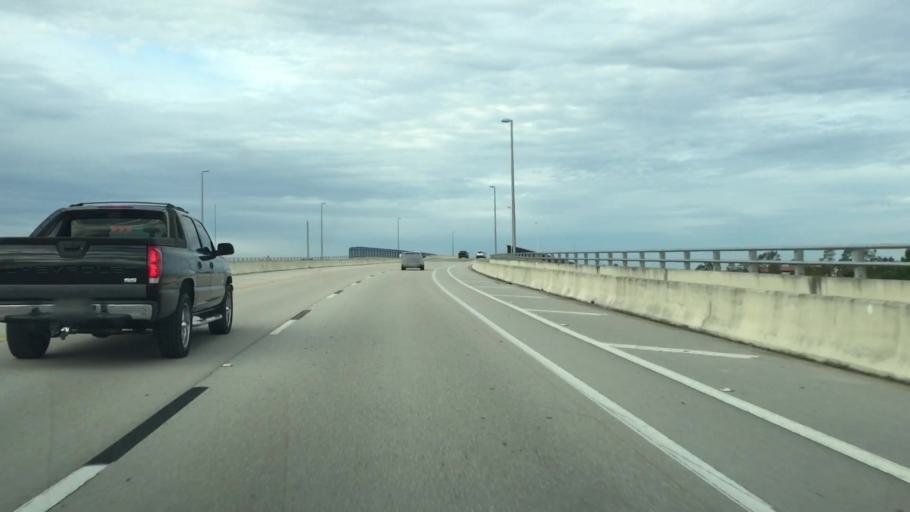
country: US
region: Florida
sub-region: Lee County
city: Three Oaks
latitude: 26.4490
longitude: -81.7808
